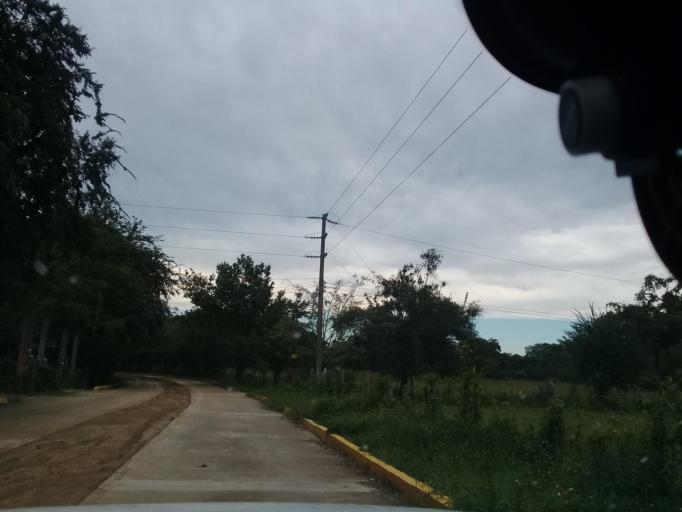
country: MX
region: Hidalgo
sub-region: Huejutla de Reyes
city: Chalahuiyapa
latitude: 21.1629
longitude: -98.3573
